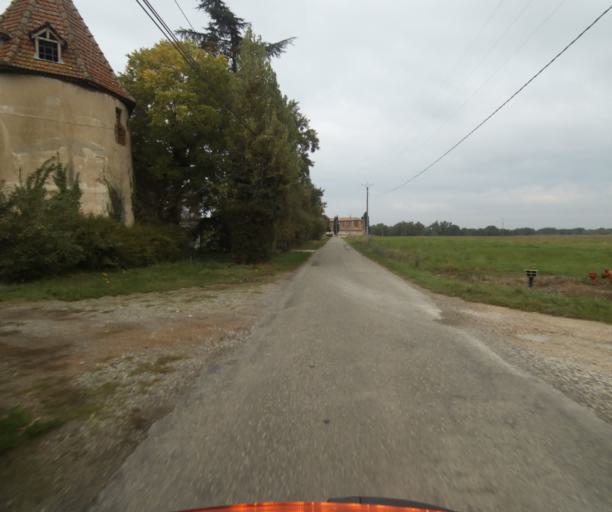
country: FR
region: Midi-Pyrenees
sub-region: Departement du Tarn-et-Garonne
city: Verdun-sur-Garonne
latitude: 43.8329
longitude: 1.1967
